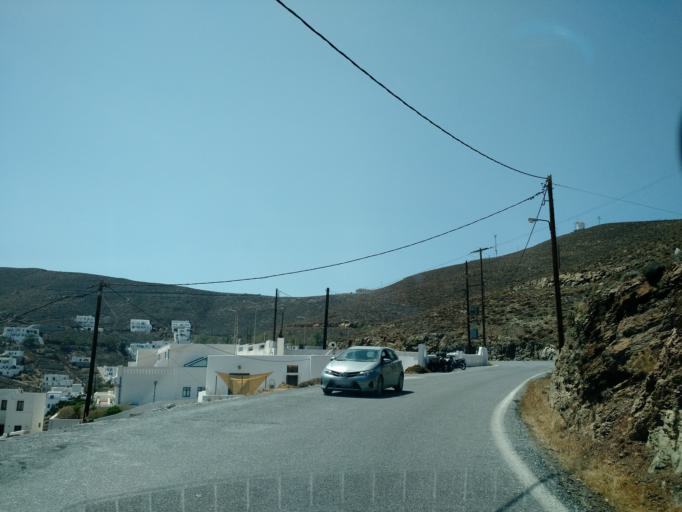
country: GR
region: South Aegean
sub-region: Nomos Dodekanisou
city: Astypalaia
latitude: 36.5501
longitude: 26.3554
